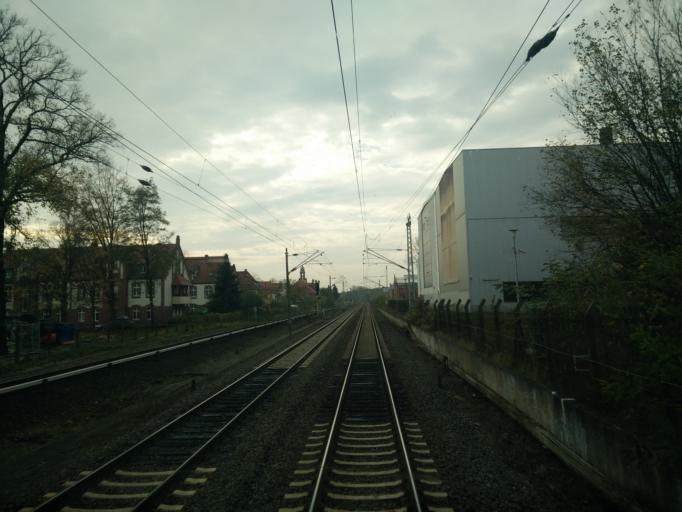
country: DE
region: Brandenburg
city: Wildau
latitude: 52.3246
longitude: 13.6357
